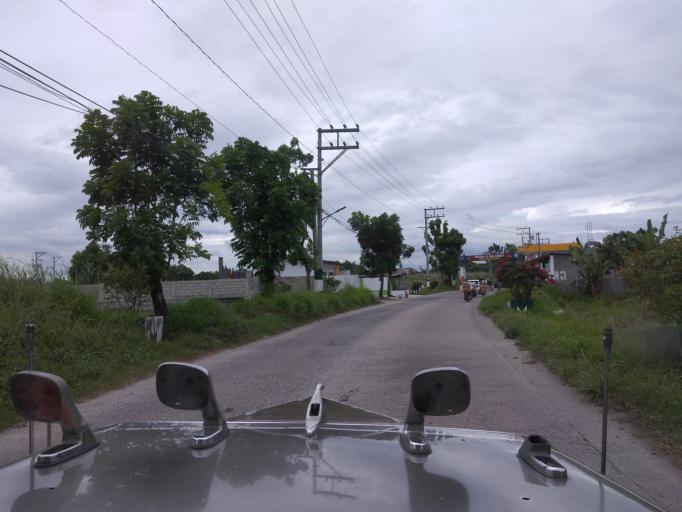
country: PH
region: Central Luzon
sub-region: Province of Pampanga
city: Pandacaqui
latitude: 15.1858
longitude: 120.6406
